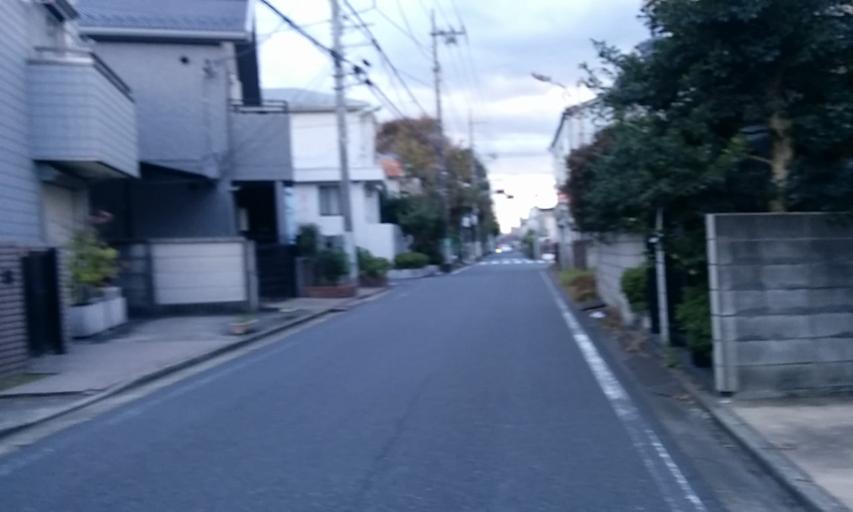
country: JP
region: Tokyo
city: Tokyo
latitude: 35.6752
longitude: 139.6384
